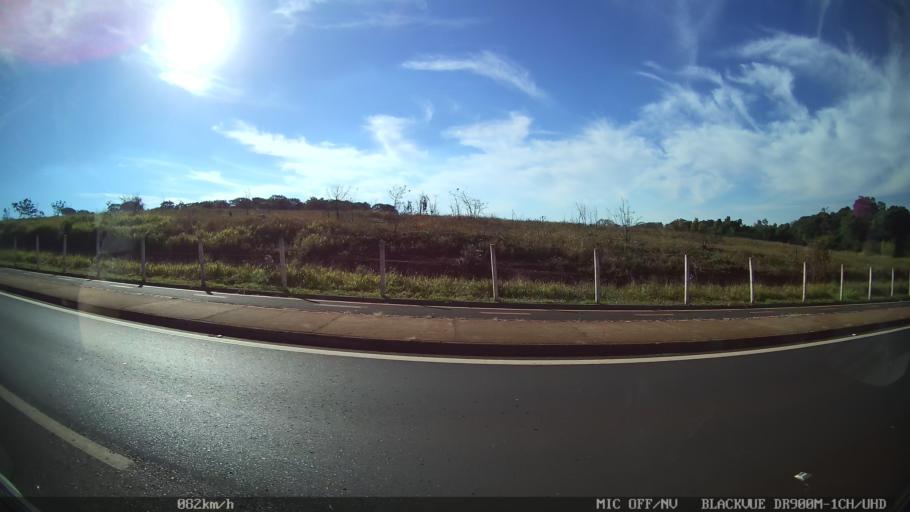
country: BR
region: Sao Paulo
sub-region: Araraquara
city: Araraquara
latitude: -21.7908
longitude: -48.1504
